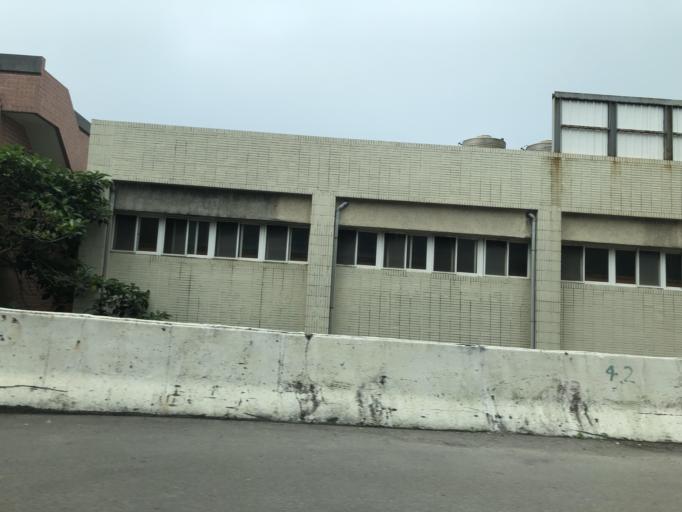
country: TW
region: Taiwan
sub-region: Keelung
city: Keelung
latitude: 25.2053
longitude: 121.6860
